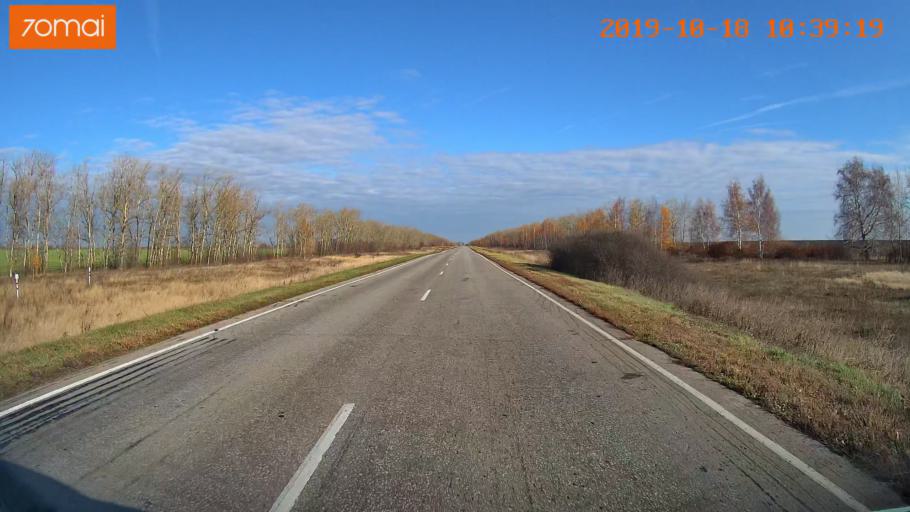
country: RU
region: Tula
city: Kurkino
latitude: 53.5852
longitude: 38.6516
